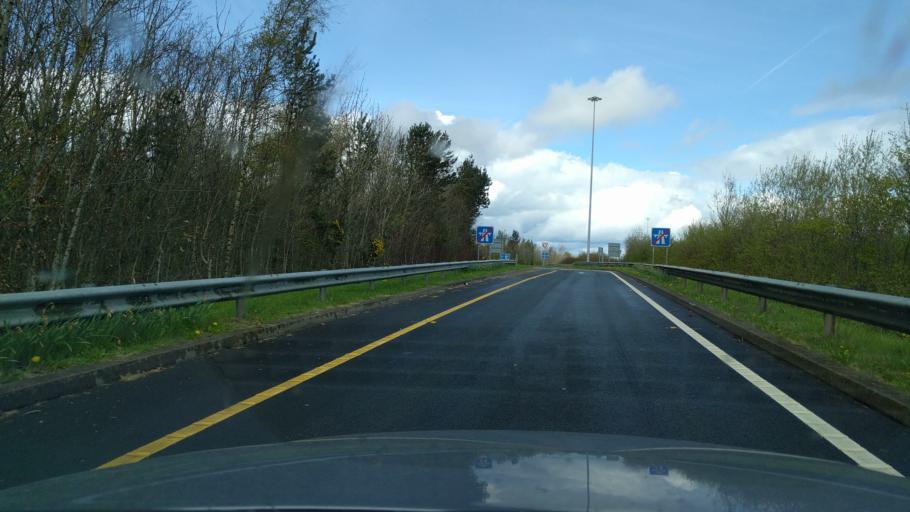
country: IE
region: Leinster
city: Balrothery
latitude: 53.5625
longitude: -6.2146
